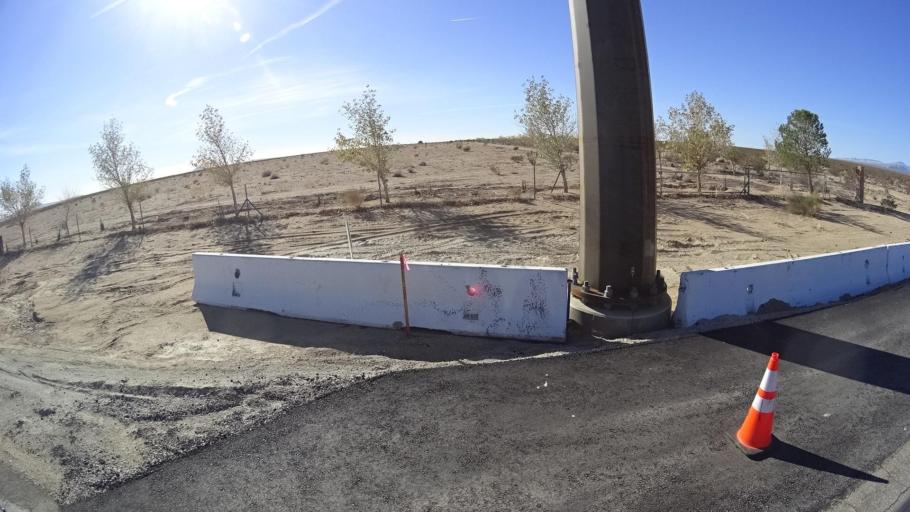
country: US
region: California
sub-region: Kern County
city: California City
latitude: 35.1986
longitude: -118.0211
